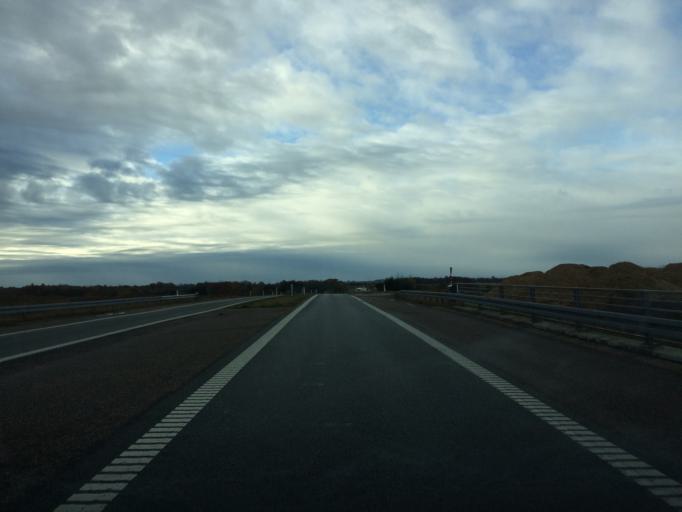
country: DK
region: Central Jutland
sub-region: Herning Kommune
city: Snejbjerg
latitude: 56.1906
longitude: 8.9016
